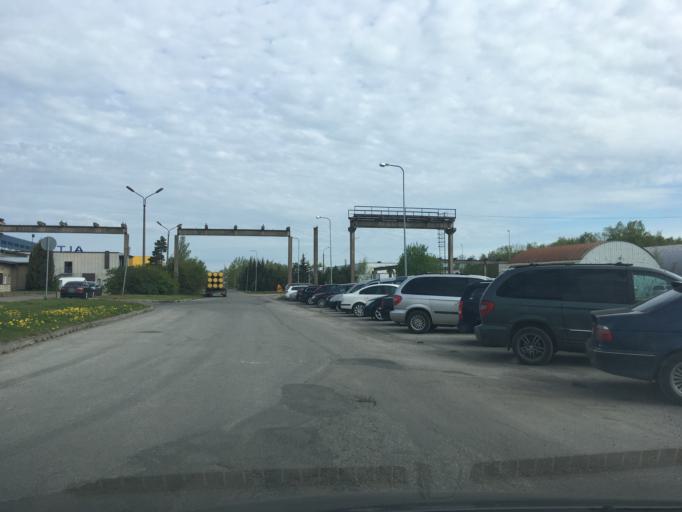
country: EE
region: Harju
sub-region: Tallinna linn
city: Kose
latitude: 59.4265
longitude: 24.8553
